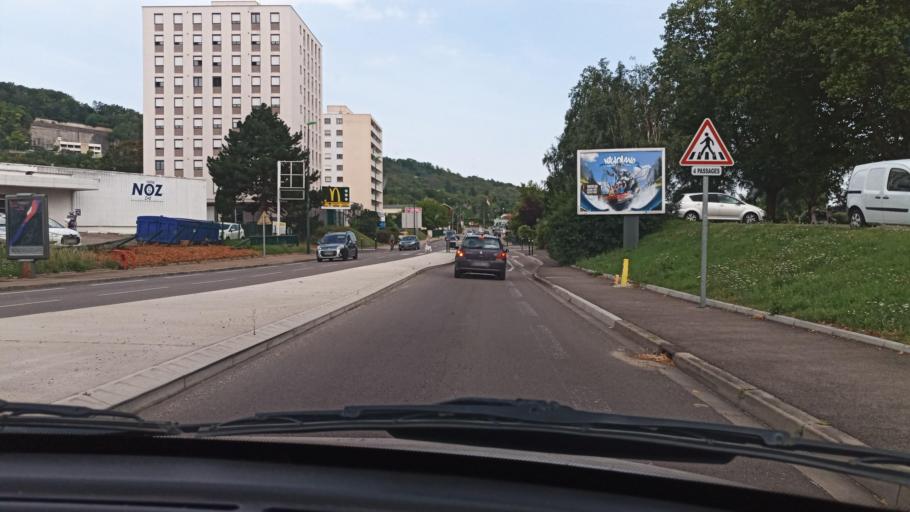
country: FR
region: Bourgogne
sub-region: Departement de l'Yonne
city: Sens
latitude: 48.1960
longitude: 3.2660
